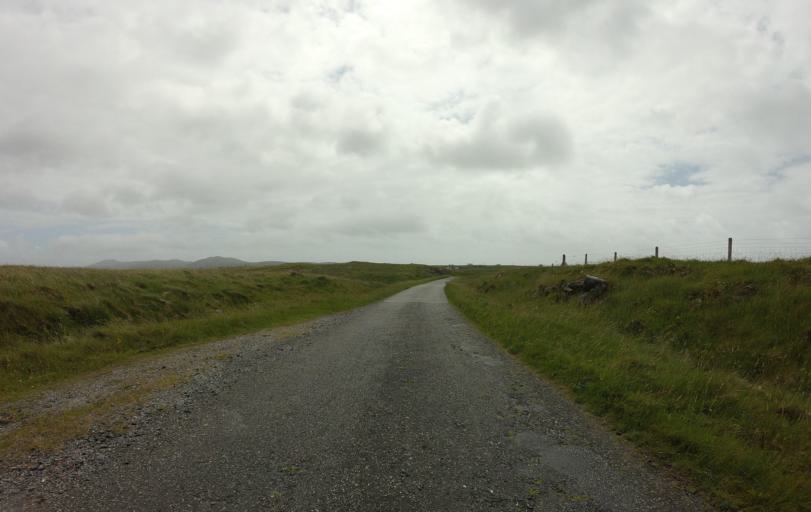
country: GB
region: Scotland
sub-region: Eilean Siar
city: Isle of South Uist
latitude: 57.2674
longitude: -7.3984
